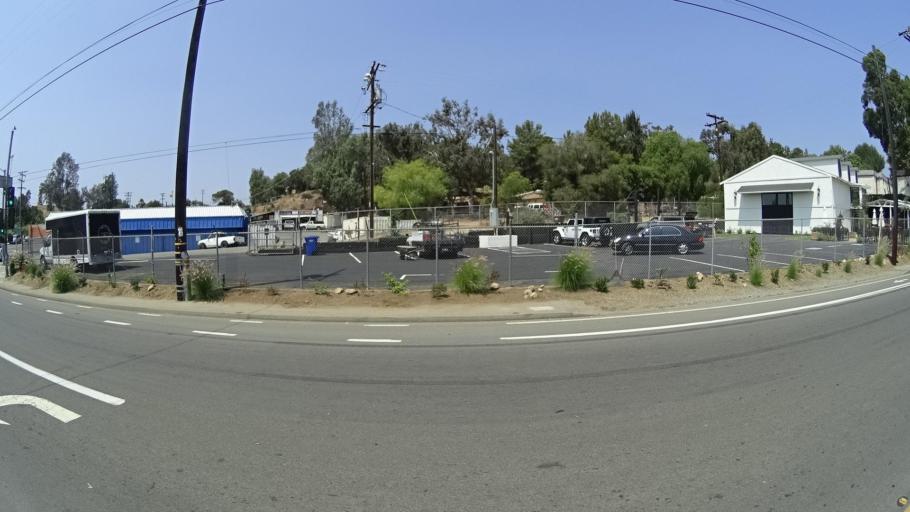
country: US
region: California
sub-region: San Diego County
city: Fallbrook
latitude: 33.3850
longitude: -117.2429
